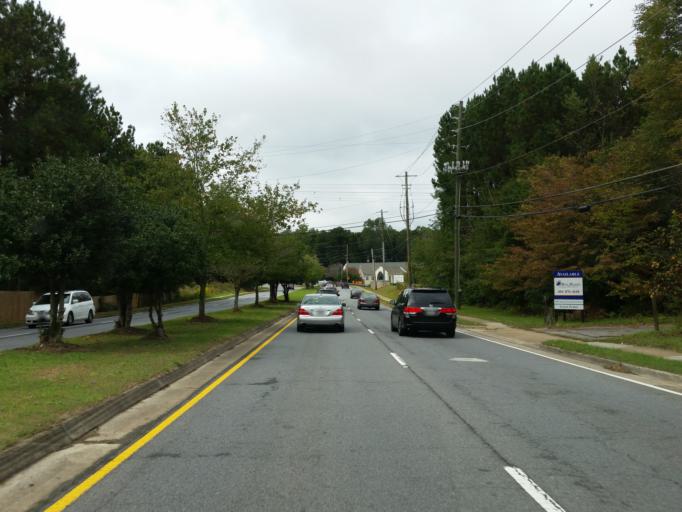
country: US
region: Georgia
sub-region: Fulton County
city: Roswell
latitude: 33.9903
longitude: -84.4276
